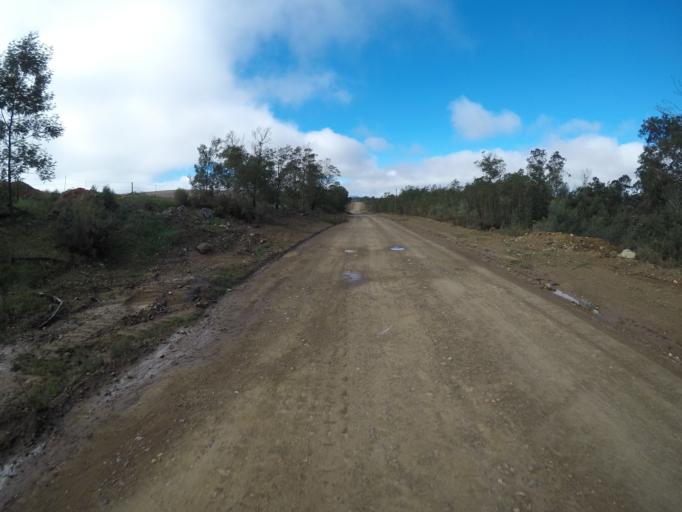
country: ZA
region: Western Cape
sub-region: Overberg District Municipality
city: Caledon
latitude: -34.1146
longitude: 19.7756
